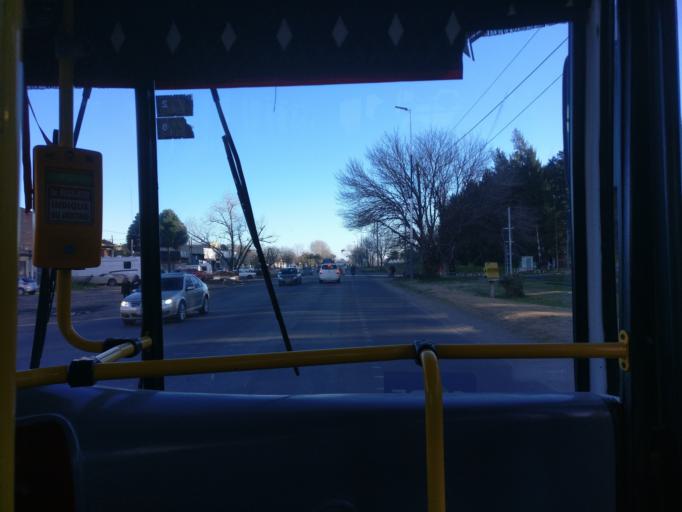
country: AR
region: Buenos Aires
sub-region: Partido de Ezeiza
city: Ezeiza
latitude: -34.8994
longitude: -58.5804
